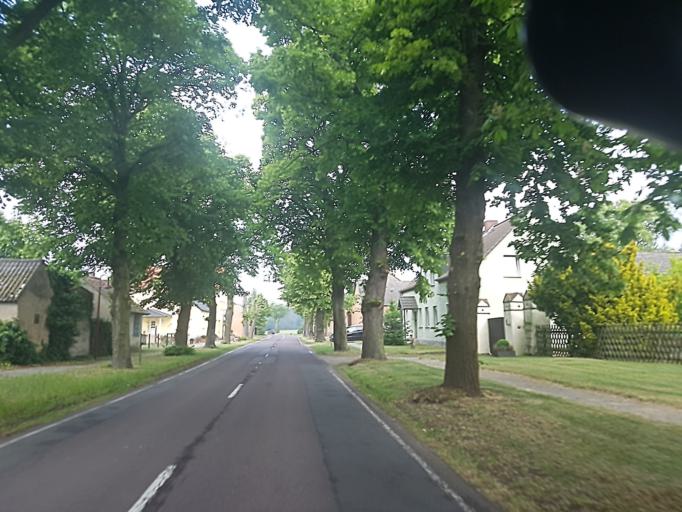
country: DE
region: Saxony-Anhalt
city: Rosslau
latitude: 51.9867
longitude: 12.3045
